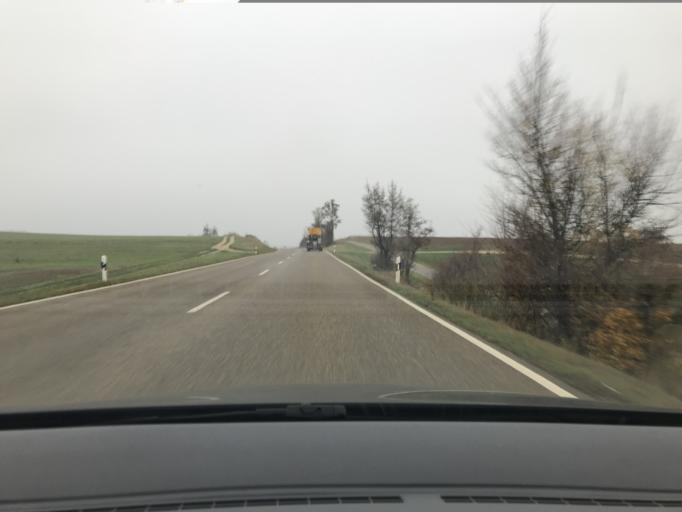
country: DE
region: Bavaria
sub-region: Swabia
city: Marktoffingen
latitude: 48.9356
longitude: 10.4619
